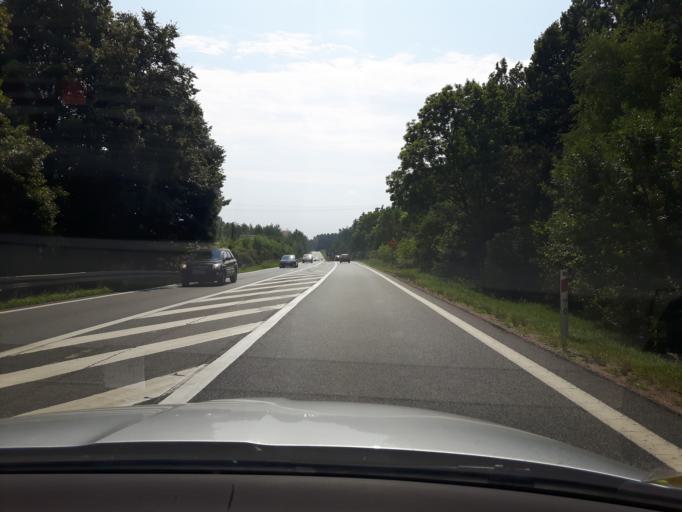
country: PL
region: Masovian Voivodeship
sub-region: Powiat mlawski
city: Mlawa
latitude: 53.1466
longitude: 20.4018
